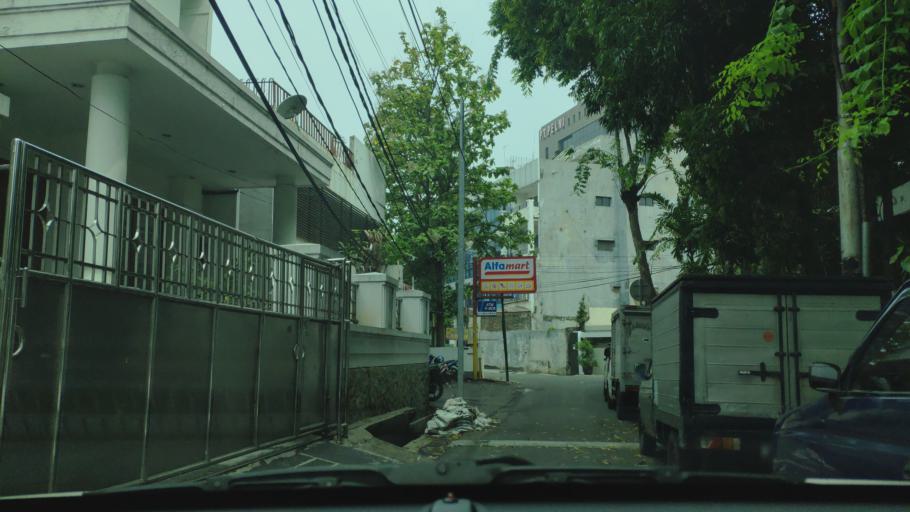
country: ID
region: Jakarta Raya
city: Jakarta
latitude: -6.1623
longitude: 106.8181
